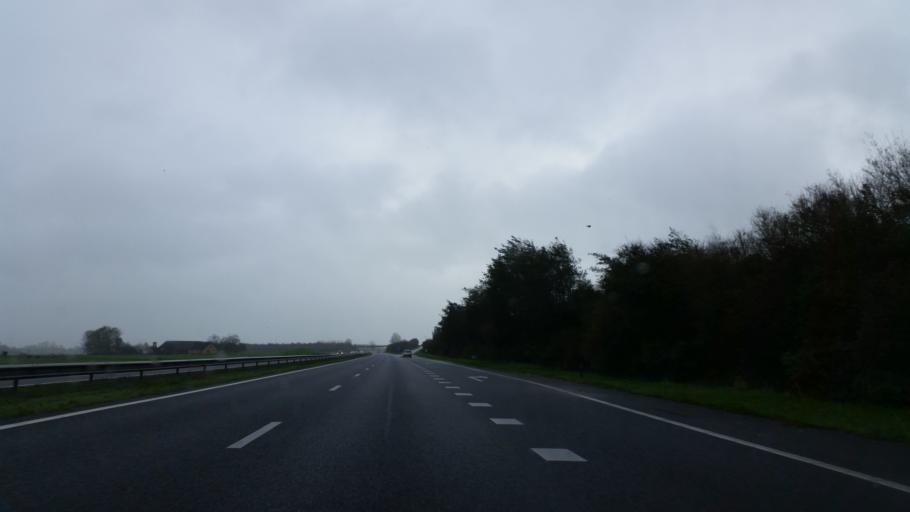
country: NL
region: Friesland
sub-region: Gemeente Boarnsterhim
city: Reduzum
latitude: 53.1186
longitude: 5.8090
